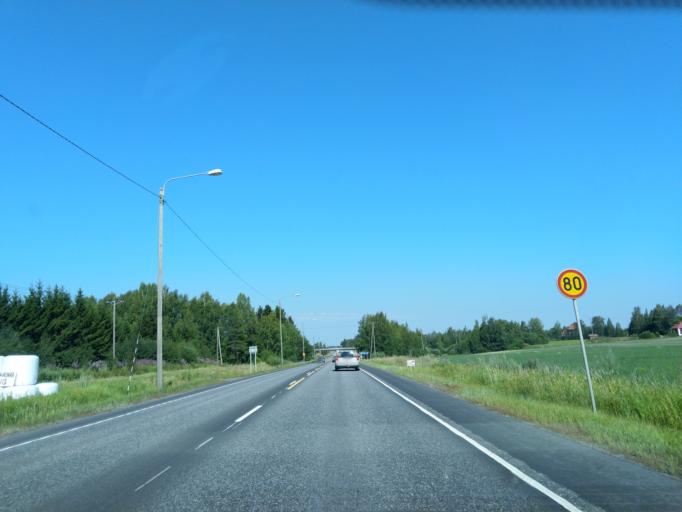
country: FI
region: Satakunta
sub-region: Pori
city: Nakkila
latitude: 61.3581
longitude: 22.0011
